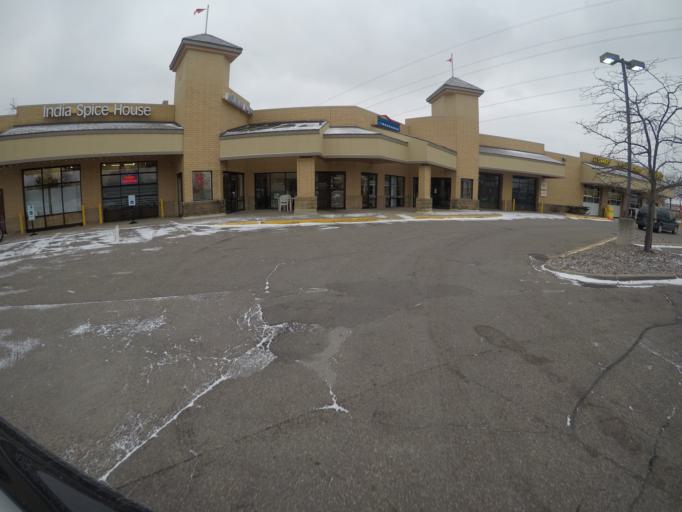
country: US
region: Minnesota
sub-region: Hennepin County
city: Eden Prairie
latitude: 44.8505
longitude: -93.4313
